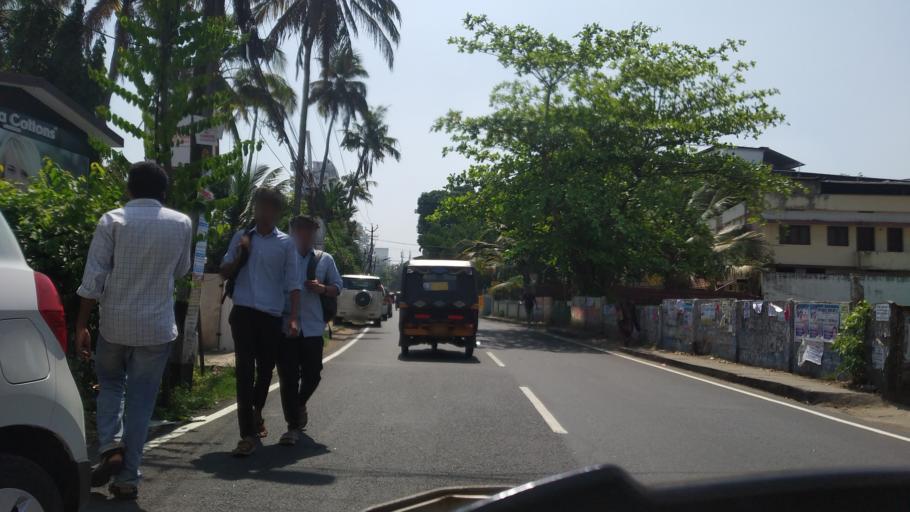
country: IN
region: Kerala
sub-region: Ernakulam
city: Elur
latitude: 10.0009
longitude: 76.3067
